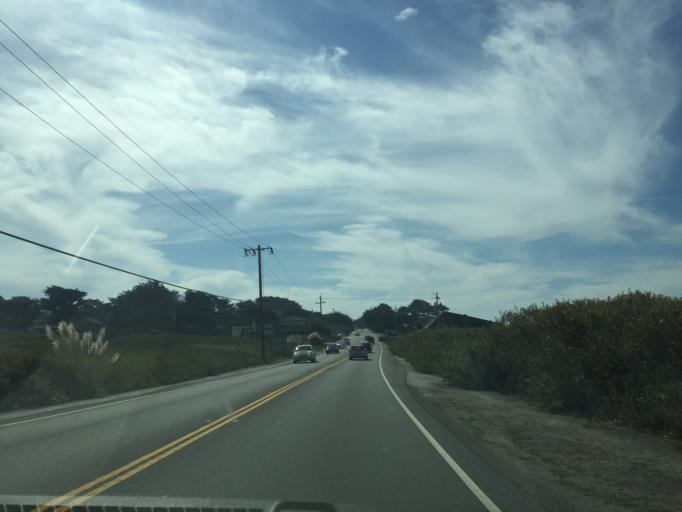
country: US
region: California
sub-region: San Mateo County
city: Montara
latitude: 37.5477
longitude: -122.5126
